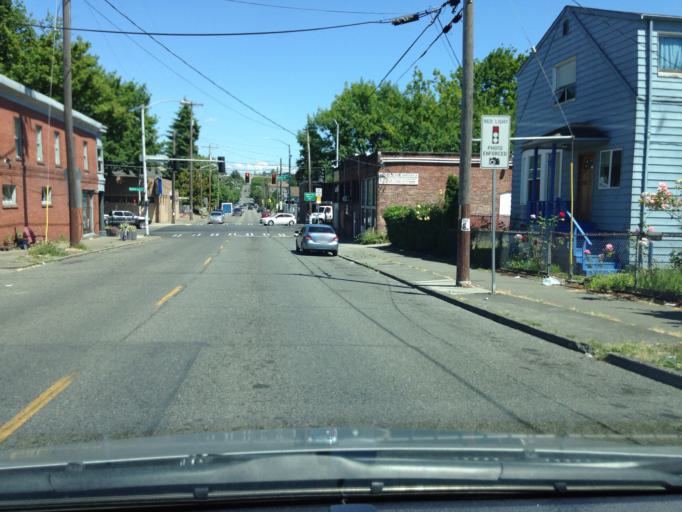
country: US
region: Washington
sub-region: King County
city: Mercer Island
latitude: 47.5512
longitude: -122.2787
